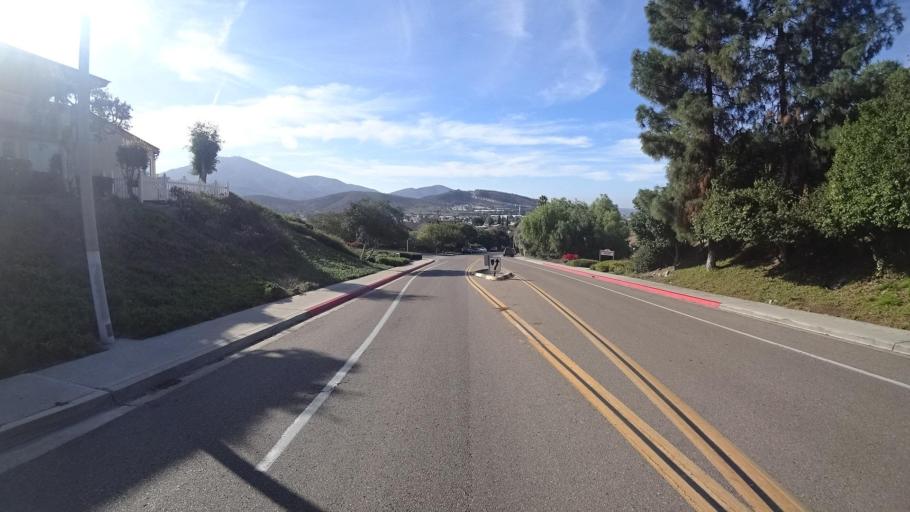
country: US
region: California
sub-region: San Diego County
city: Rancho San Diego
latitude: 32.7359
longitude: -116.9613
